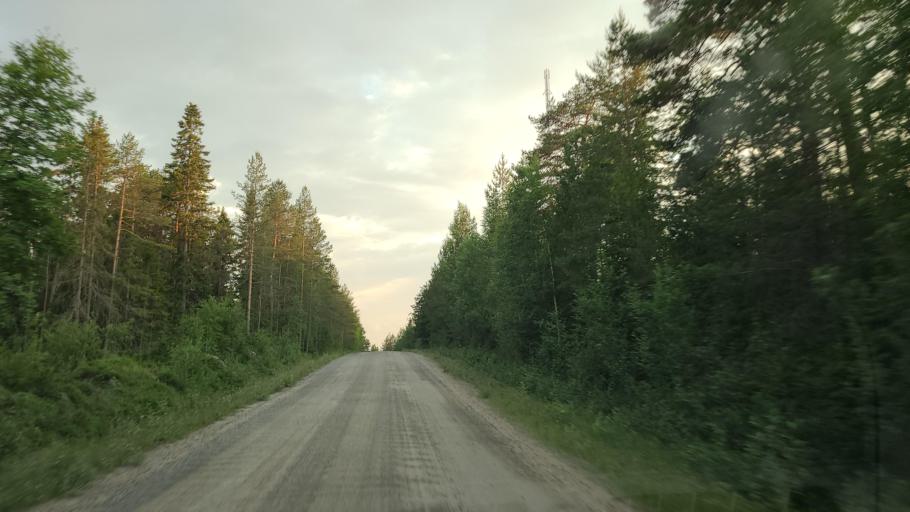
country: SE
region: Vaesterbotten
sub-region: Robertsfors Kommun
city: Robertsfors
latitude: 64.0704
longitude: 20.8780
